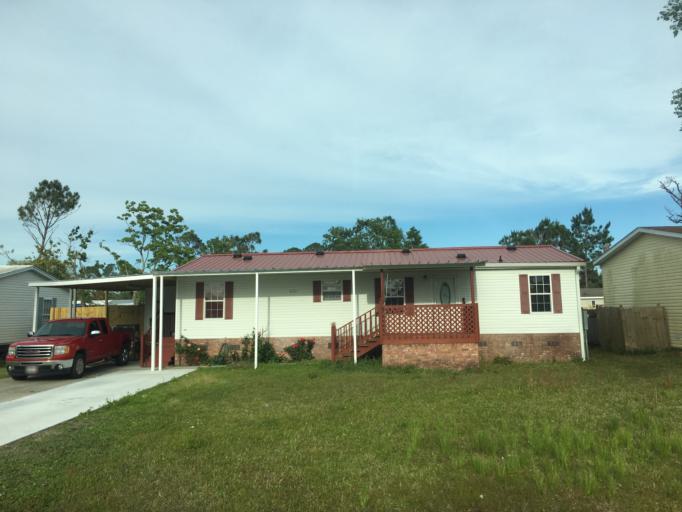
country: US
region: Florida
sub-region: Bay County
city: Upper Grand Lagoon
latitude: 30.1666
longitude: -85.7655
